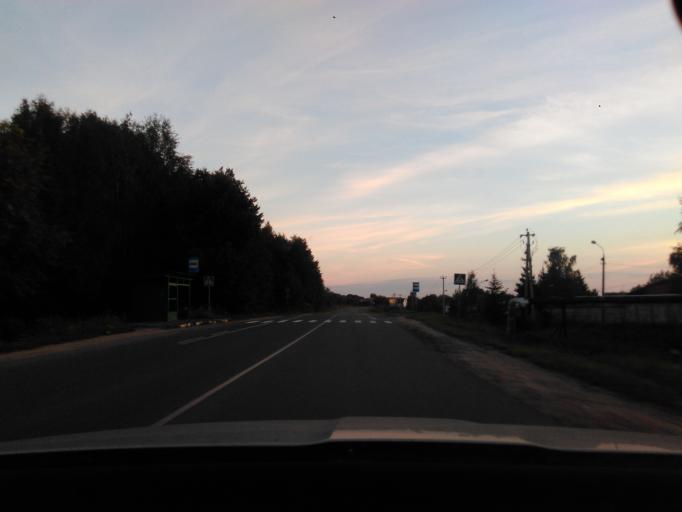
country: RU
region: Moskovskaya
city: Klin
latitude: 56.2875
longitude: 36.7880
